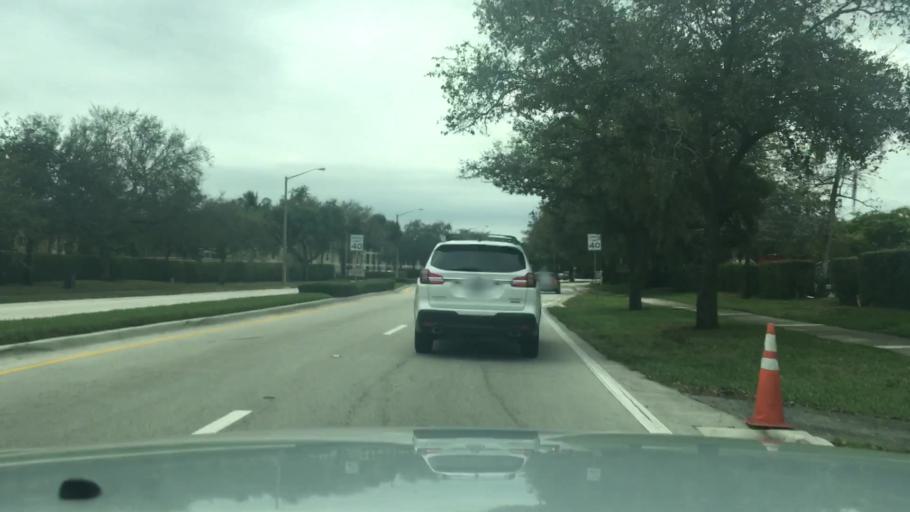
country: US
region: Florida
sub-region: Broward County
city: Tamarac
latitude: 26.2430
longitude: -80.2430
